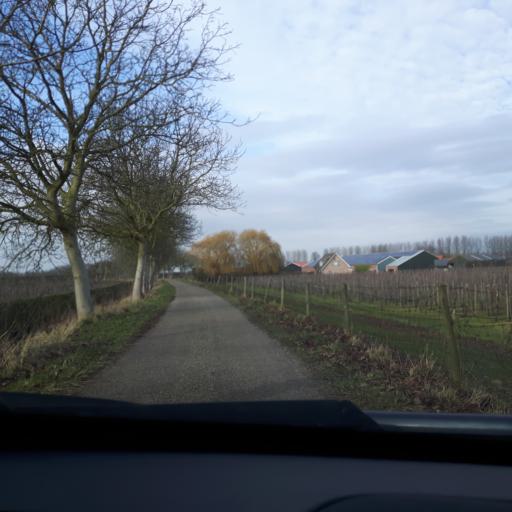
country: NL
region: Zeeland
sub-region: Gemeente Goes
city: Goes
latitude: 51.4439
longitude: 3.9105
